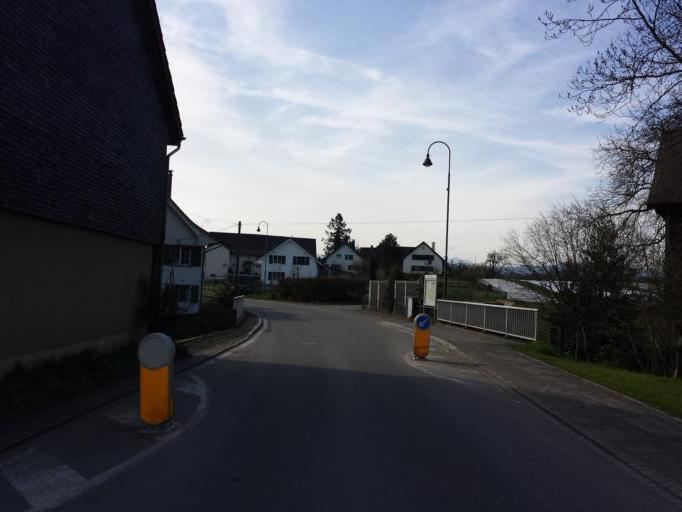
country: CH
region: Thurgau
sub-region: Arbon District
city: Salmsach
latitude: 47.5507
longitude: 9.3569
